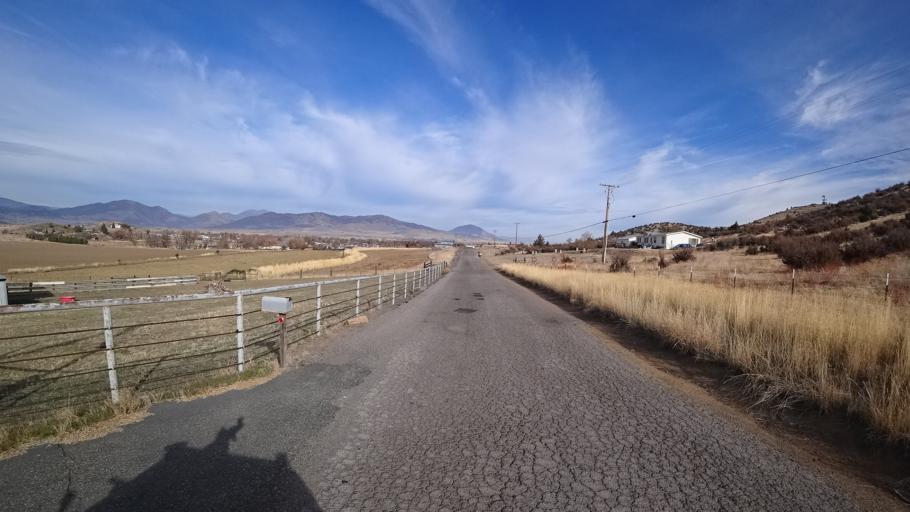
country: US
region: California
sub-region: Siskiyou County
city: Montague
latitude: 41.7160
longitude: -122.5215
